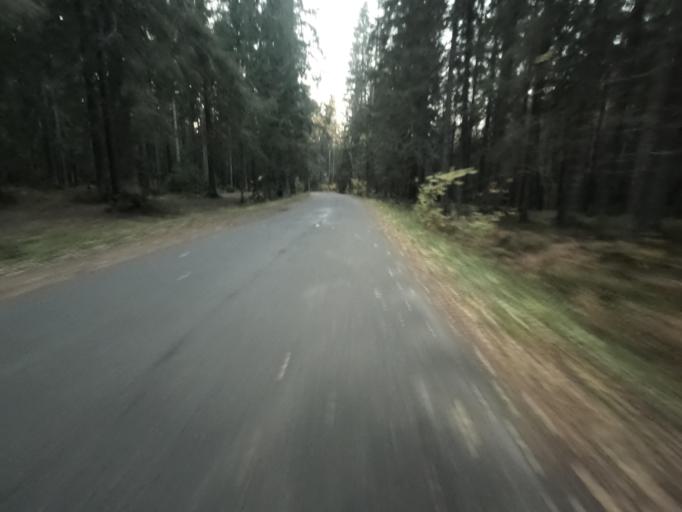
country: RU
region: St.-Petersburg
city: Komarovo
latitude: 60.2072
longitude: 29.7911
